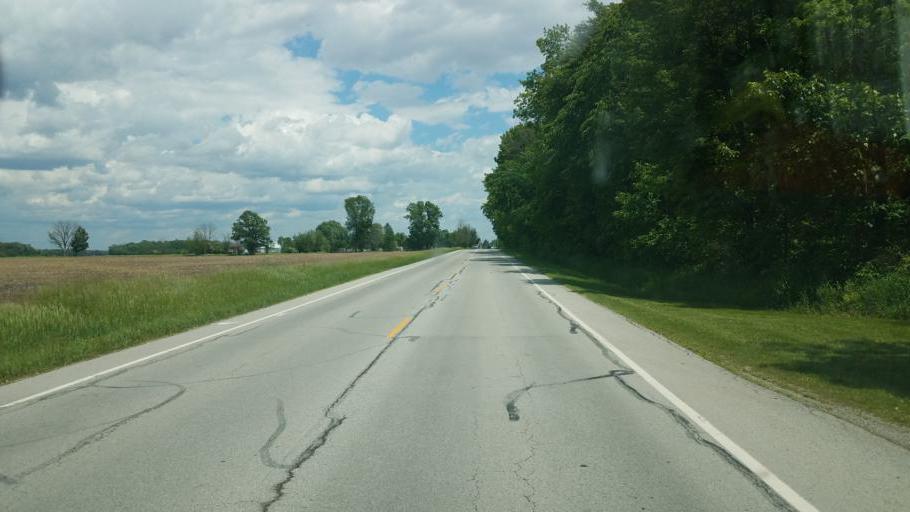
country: US
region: Ohio
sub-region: Crawford County
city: Crestline
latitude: 40.8067
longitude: -82.7820
